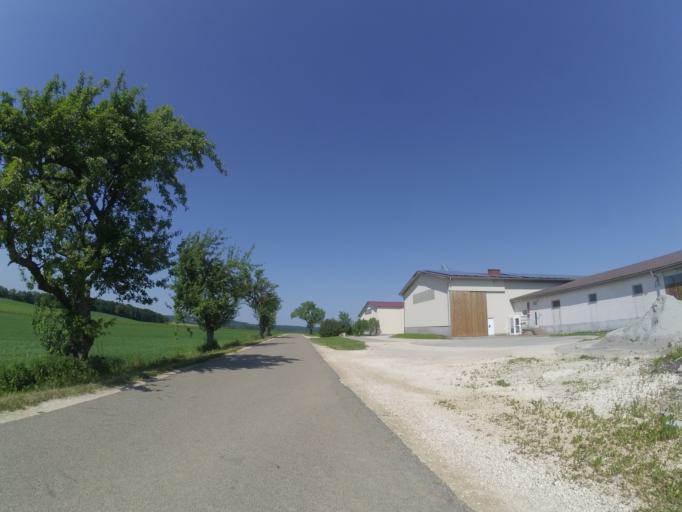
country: DE
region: Baden-Wuerttemberg
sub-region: Tuebingen Region
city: Amstetten
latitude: 48.5723
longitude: 9.8428
